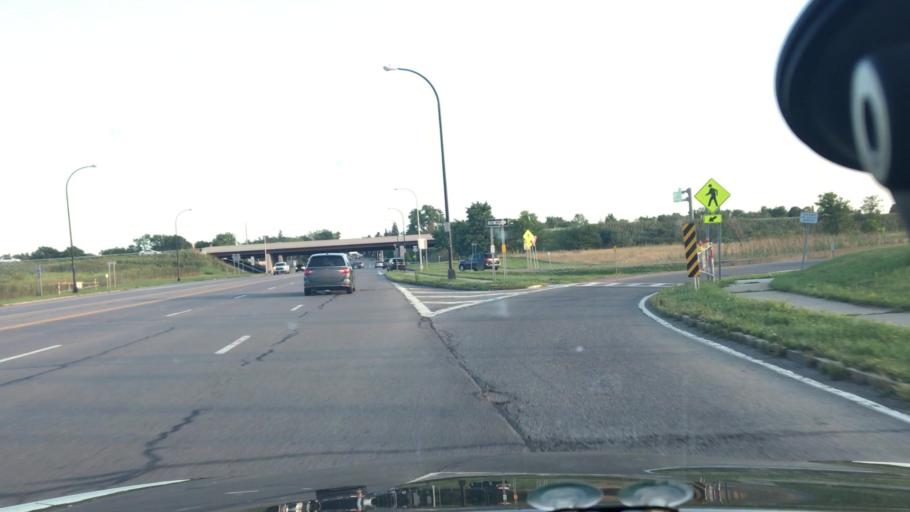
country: US
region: New York
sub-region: Erie County
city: Tonawanda
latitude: 42.9976
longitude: -78.8749
